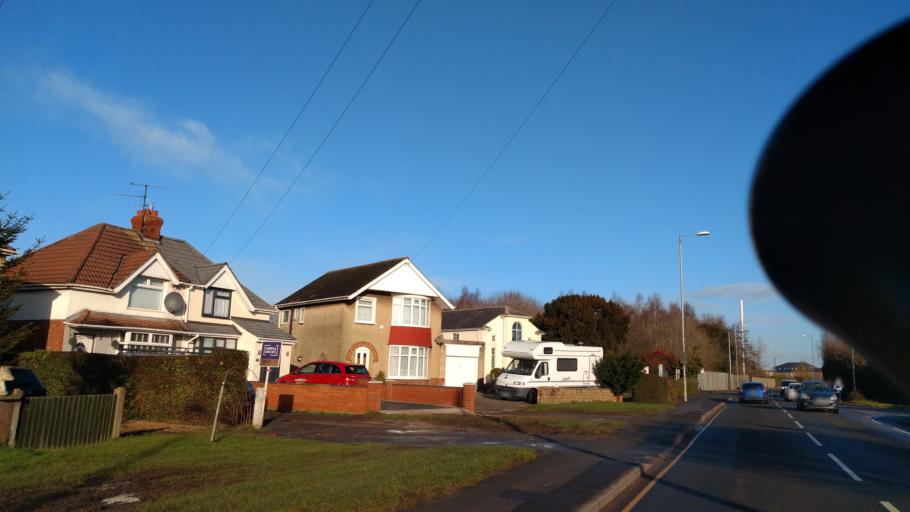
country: GB
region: England
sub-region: Borough of Swindon
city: Swindon
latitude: 51.5782
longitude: -1.7524
